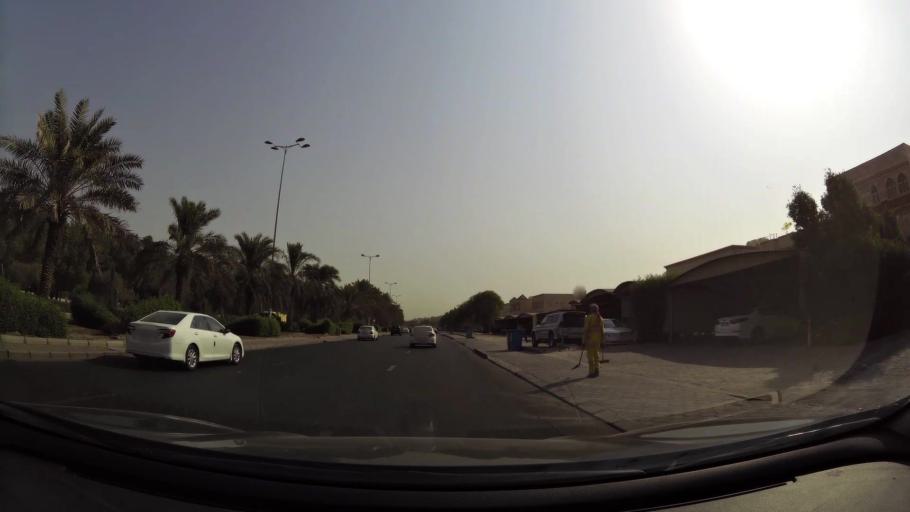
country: KW
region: Al Asimah
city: Ar Rabiyah
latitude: 29.2744
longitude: 47.8842
